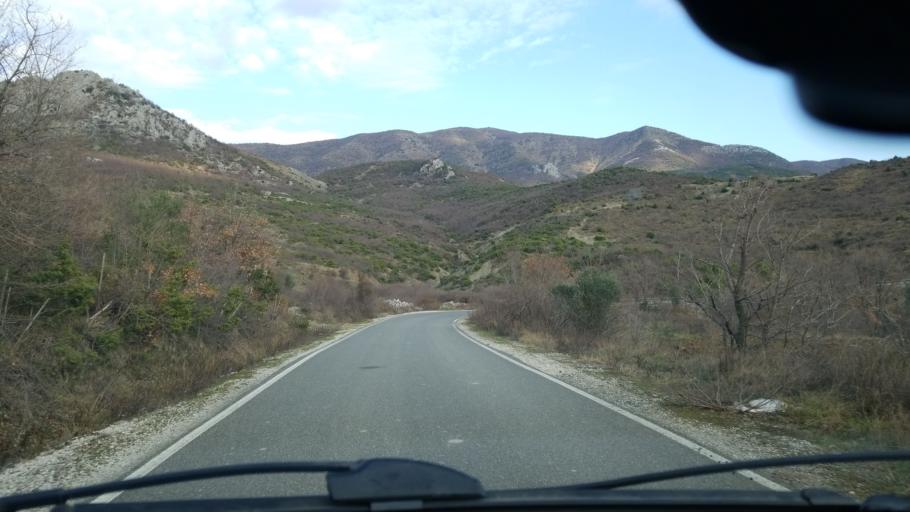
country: AL
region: Lezhe
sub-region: Rrethi i Lezhes
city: Kallmeti i Madh
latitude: 41.8787
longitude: 19.6947
